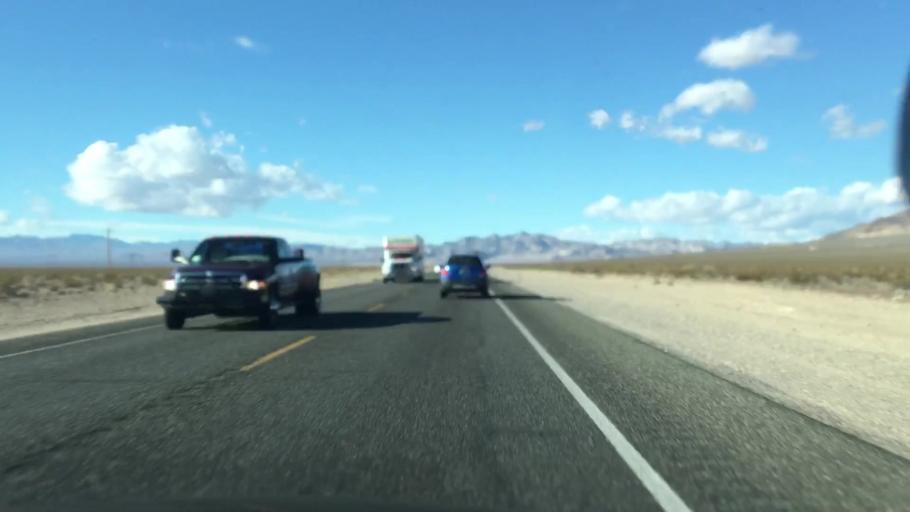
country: US
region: Nevada
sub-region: Nye County
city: Beatty
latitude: 36.7920
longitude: -116.7068
